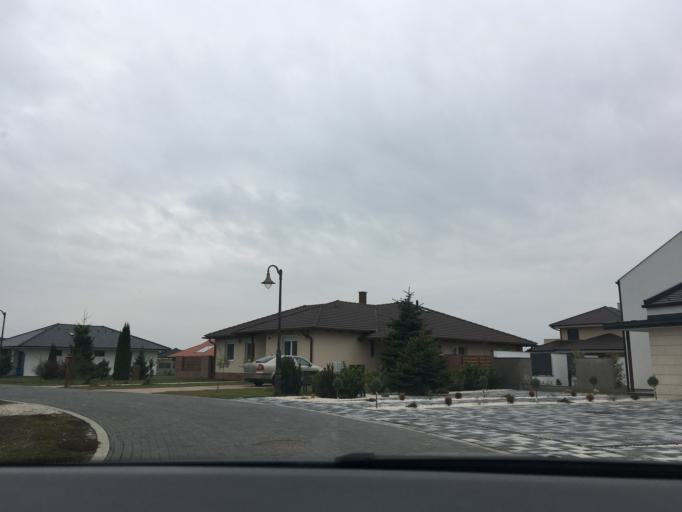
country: HU
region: Hajdu-Bihar
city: Debrecen
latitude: 47.5527
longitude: 21.6895
